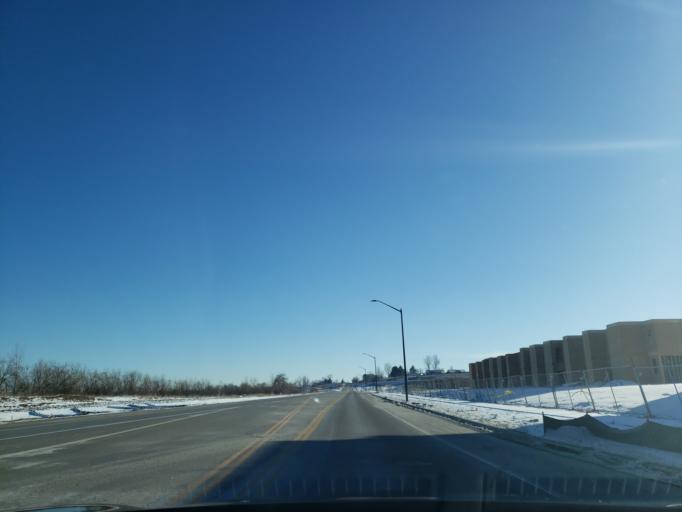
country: US
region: Colorado
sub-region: Larimer County
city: Fort Collins
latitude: 40.5211
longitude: -105.0013
